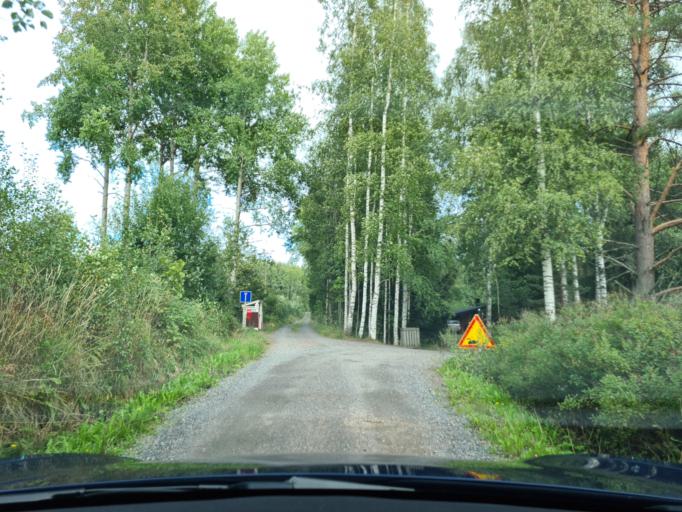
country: FI
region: Uusimaa
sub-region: Helsinki
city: Vihti
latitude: 60.4181
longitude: 24.4967
